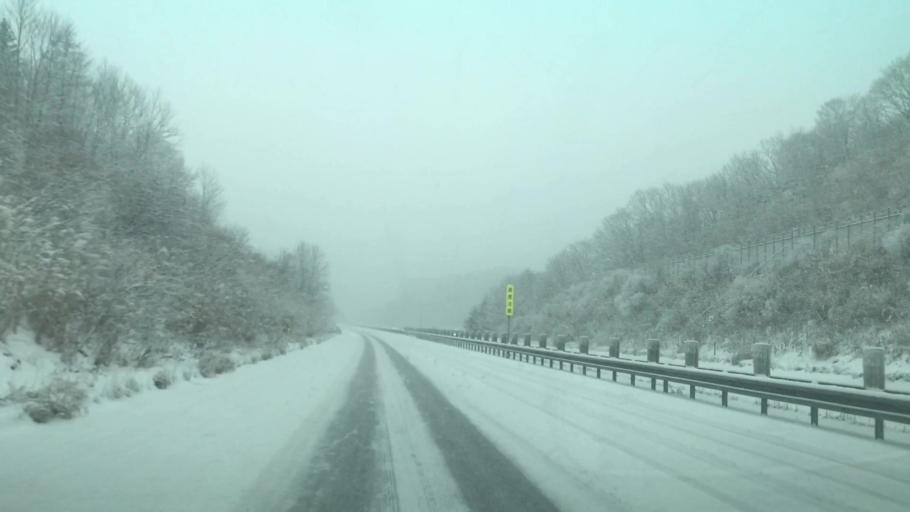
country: JP
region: Hokkaido
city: Muroran
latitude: 42.4287
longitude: 141.0993
